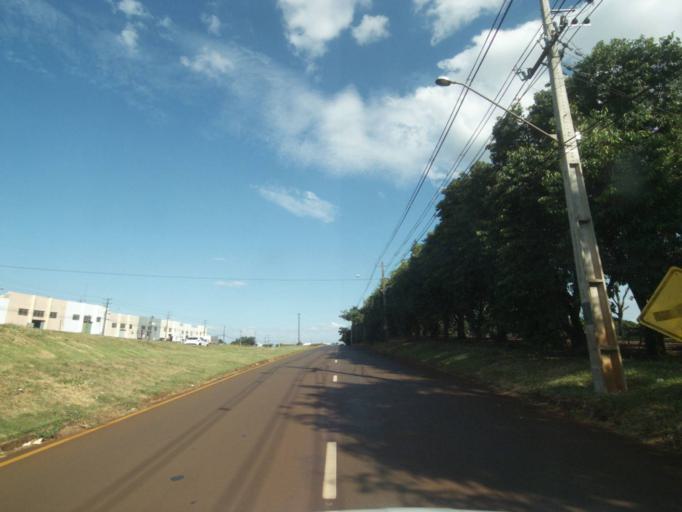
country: BR
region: Parana
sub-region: Londrina
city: Londrina
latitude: -23.3485
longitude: -51.1699
